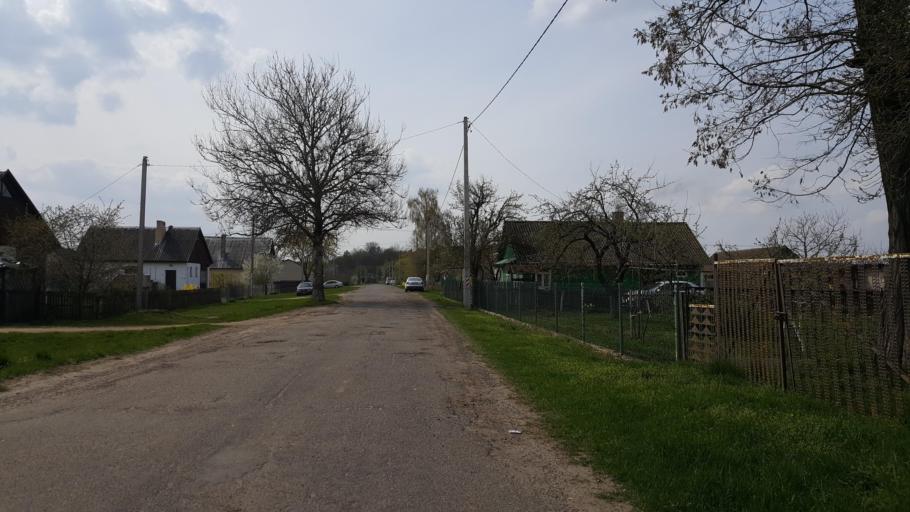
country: BY
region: Brest
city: Zhabinka
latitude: 52.2197
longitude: 23.9284
